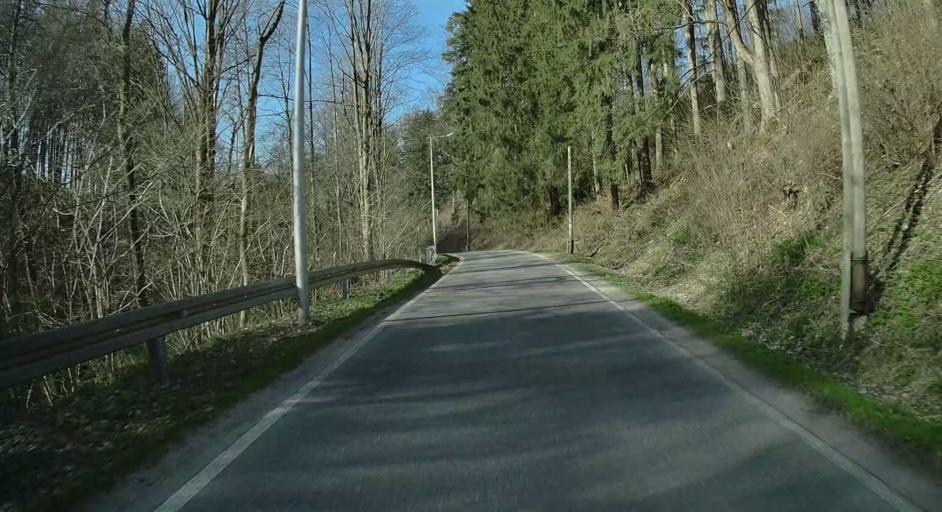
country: PL
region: Lower Silesian Voivodeship
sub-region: Powiat klodzki
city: Lewin Klodzki
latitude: 50.3937
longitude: 16.3012
